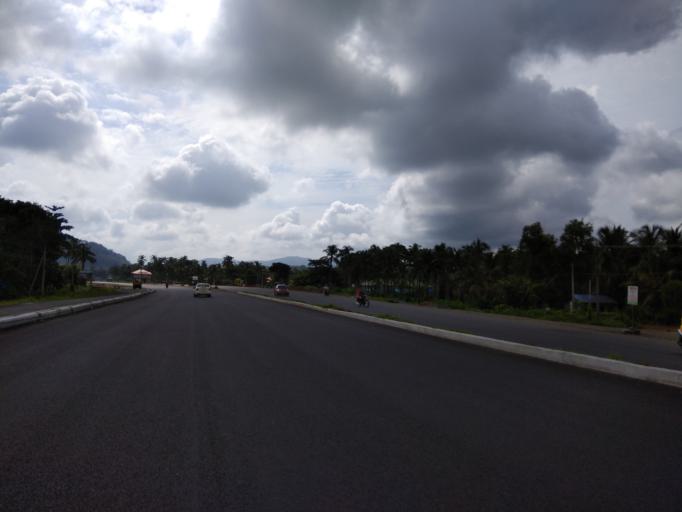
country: IN
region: Kerala
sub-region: Thrissur District
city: Trichur
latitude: 10.5543
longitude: 76.3164
